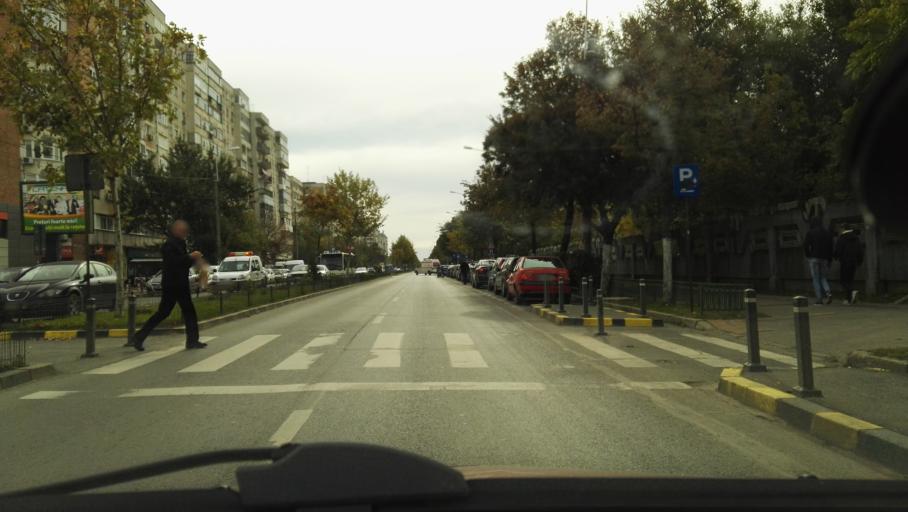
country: RO
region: Ilfov
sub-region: Comuna Popesti-Leordeni
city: Popesti-Leordeni
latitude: 44.3852
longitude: 26.1294
